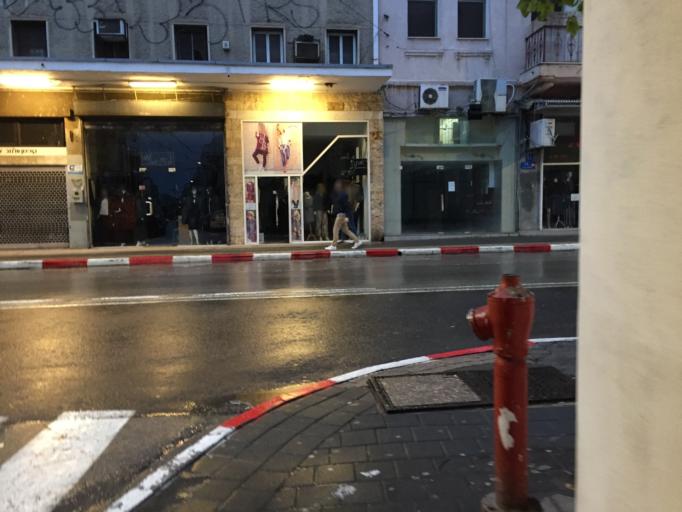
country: IL
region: Tel Aviv
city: Yafo
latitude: 32.0602
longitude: 34.7696
